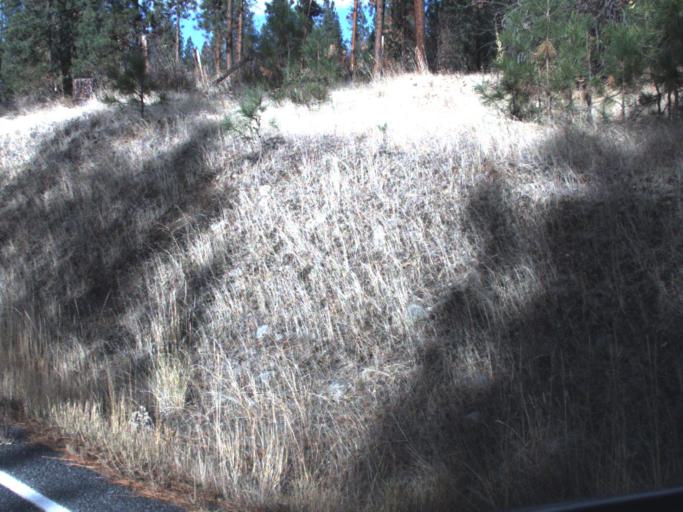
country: US
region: Washington
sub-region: Stevens County
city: Kettle Falls
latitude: 48.2905
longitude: -118.1414
